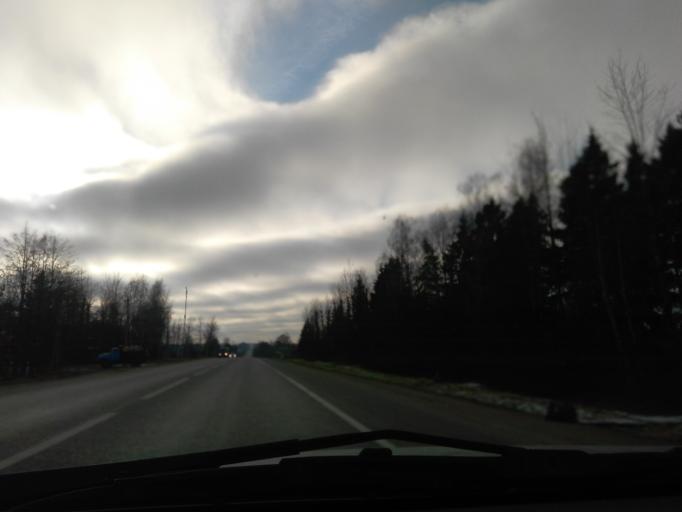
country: RU
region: Moskovskaya
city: Troitsk
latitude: 55.3105
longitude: 37.1487
